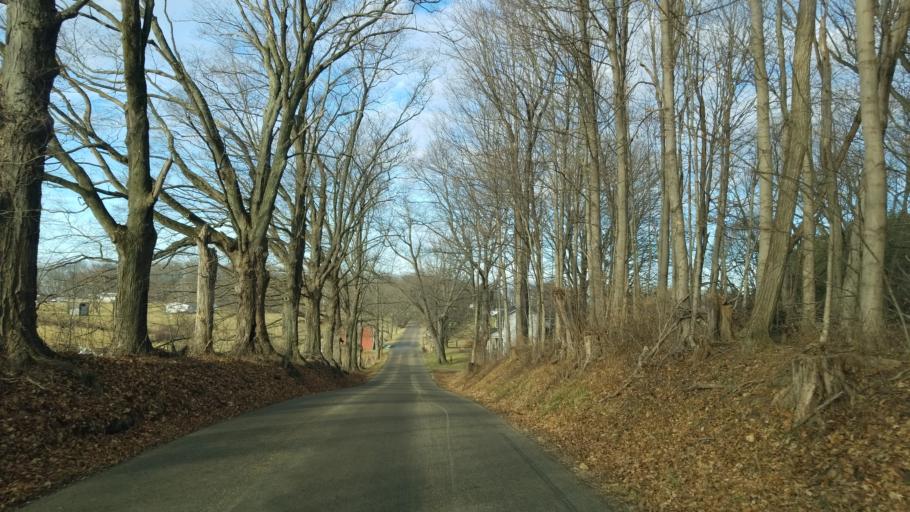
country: US
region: Ohio
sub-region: Knox County
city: Gambier
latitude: 40.3161
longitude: -82.3614
